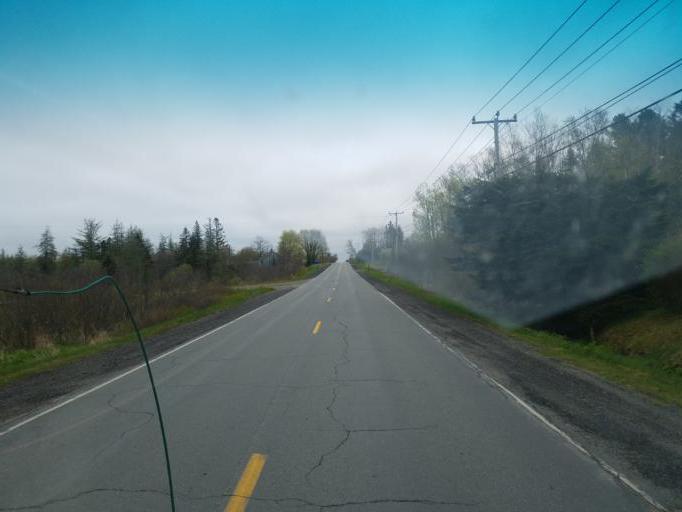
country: US
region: Maine
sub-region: Washington County
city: Eastport
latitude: 44.8319
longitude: -67.0335
